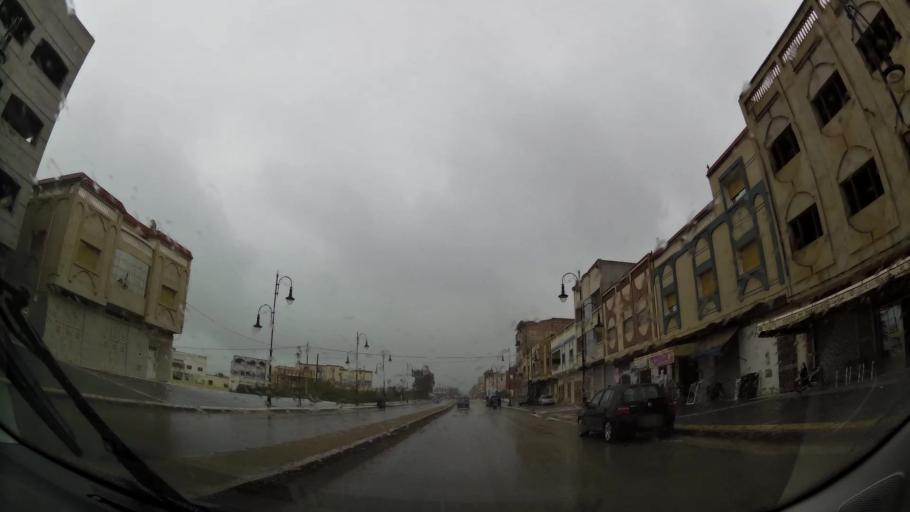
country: MA
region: Taza-Al Hoceima-Taounate
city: Imzourene
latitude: 35.1167
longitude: -3.8420
